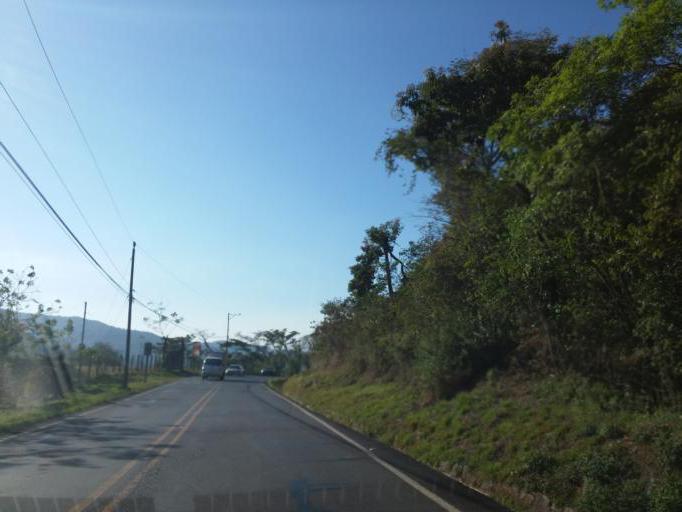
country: CR
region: Heredia
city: Colon
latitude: 9.8910
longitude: -84.2272
